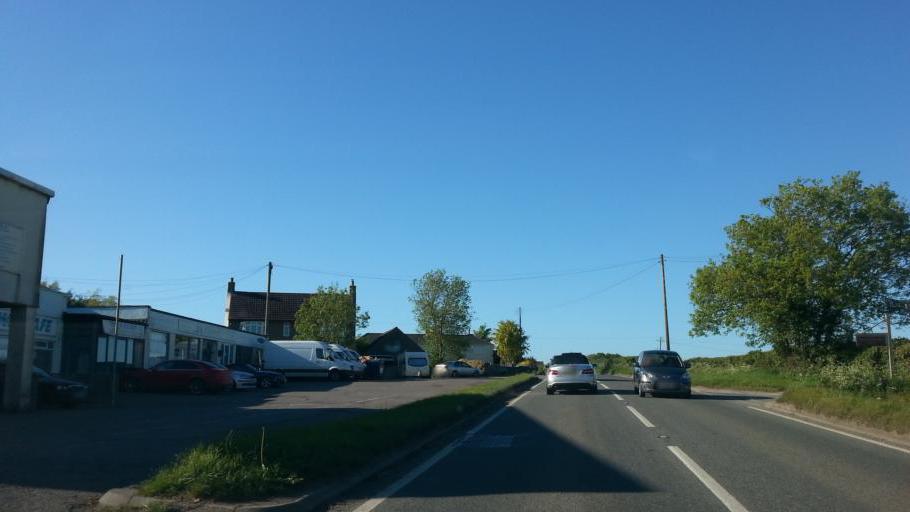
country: GB
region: England
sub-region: Somerset
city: Evercreech
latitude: 51.1280
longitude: -2.5161
